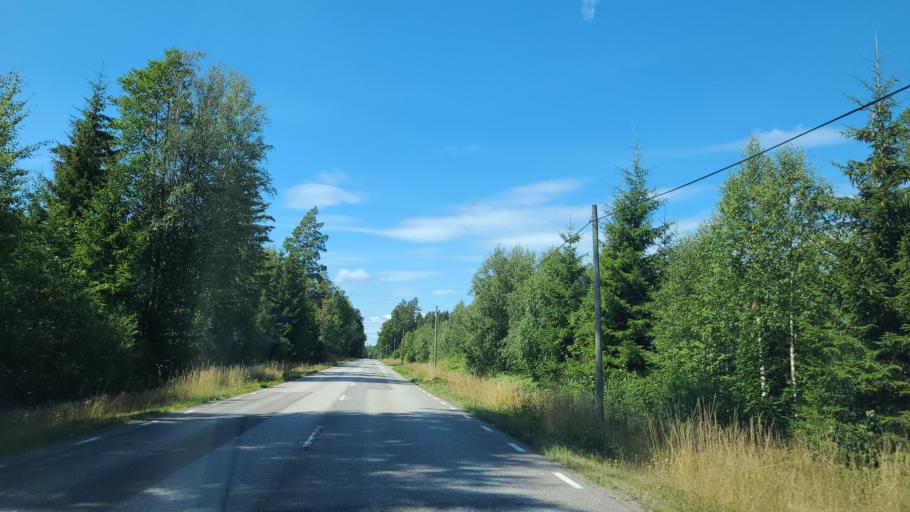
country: SE
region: Kalmar
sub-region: Nybro Kommun
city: Nybro
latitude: 56.5635
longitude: 15.7871
